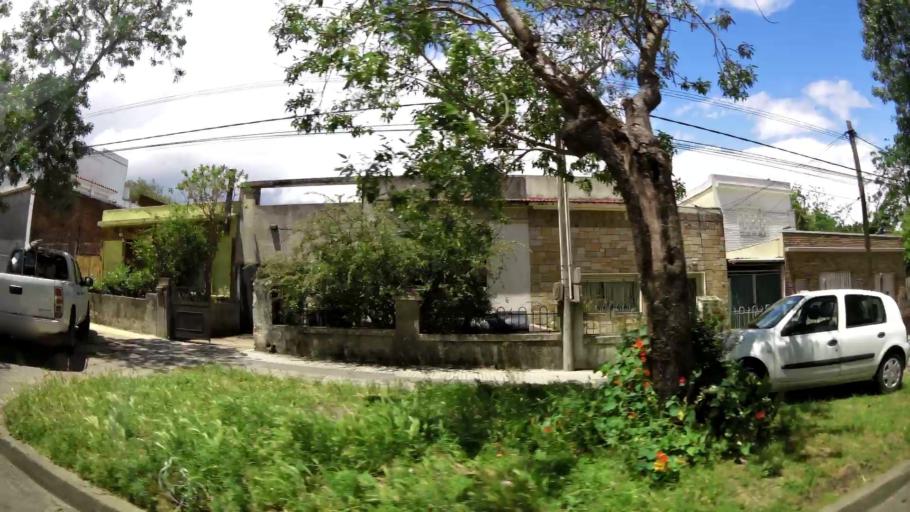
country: UY
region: Montevideo
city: Montevideo
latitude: -34.8583
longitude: -56.1847
